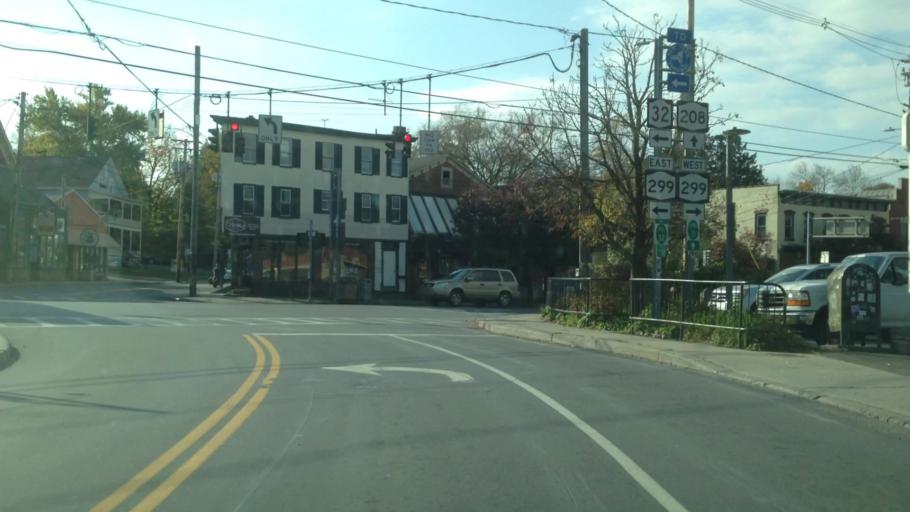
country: US
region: New York
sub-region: Ulster County
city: New Paltz
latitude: 41.7478
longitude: -74.0869
